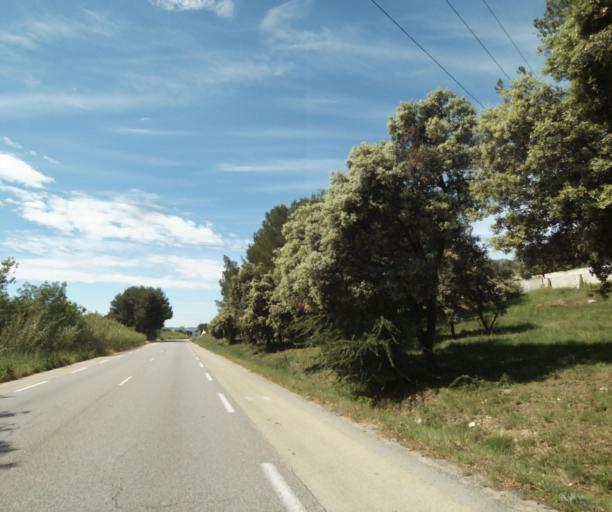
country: FR
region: Provence-Alpes-Cote d'Azur
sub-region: Departement des Bouches-du-Rhone
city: Rognac
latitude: 43.5070
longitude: 5.2235
